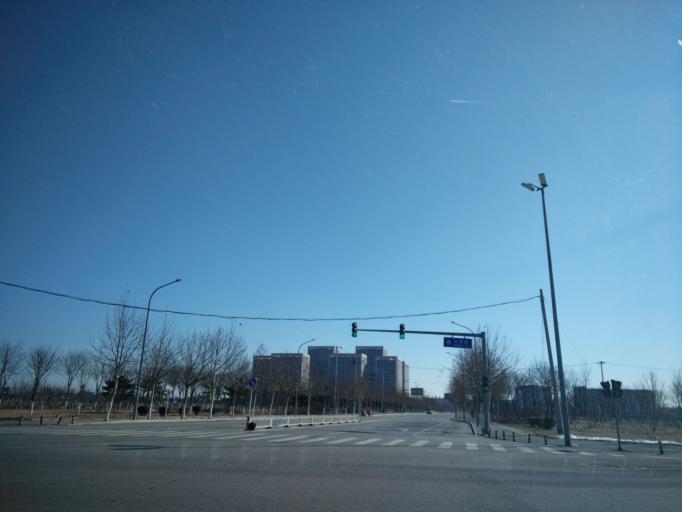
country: CN
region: Beijing
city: Yinghai
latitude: 39.7509
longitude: 116.4893
